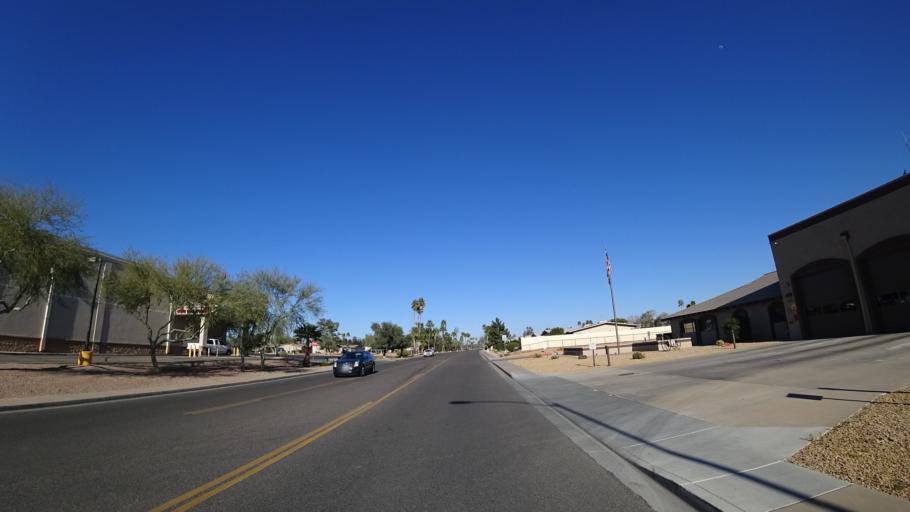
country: US
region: Arizona
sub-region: Maricopa County
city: Sun City West
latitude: 33.6573
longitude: -112.3503
